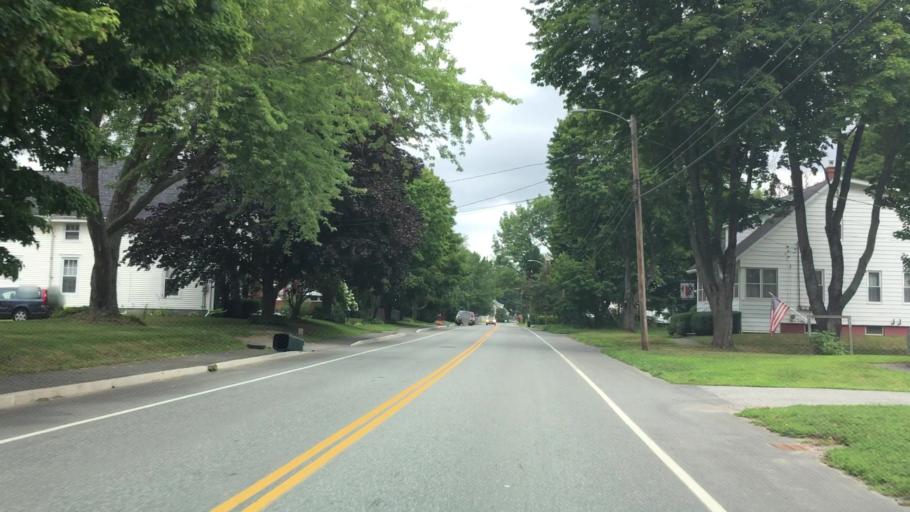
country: US
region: Maine
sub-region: Penobscot County
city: Brewer
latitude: 44.7667
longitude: -68.7760
